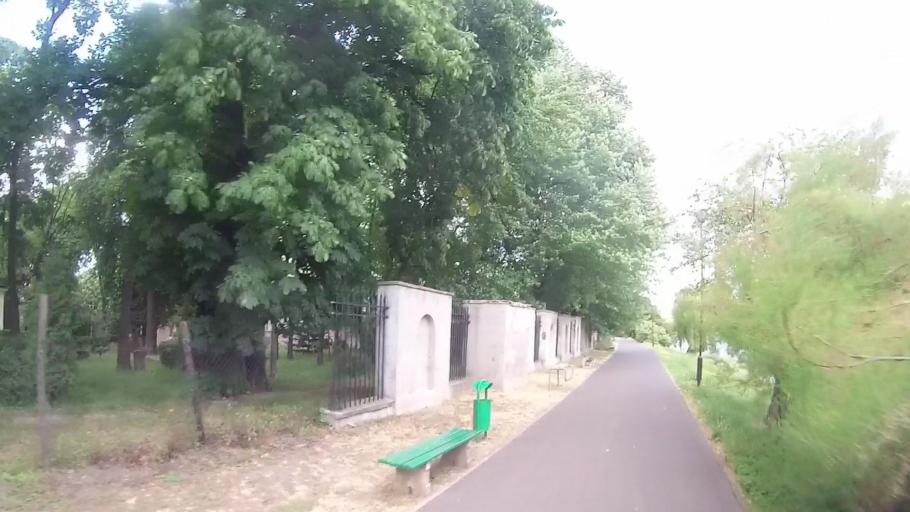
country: PL
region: Masovian Voivodeship
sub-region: Warszawa
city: Praga Polnoc
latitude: 52.2458
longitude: 21.0529
